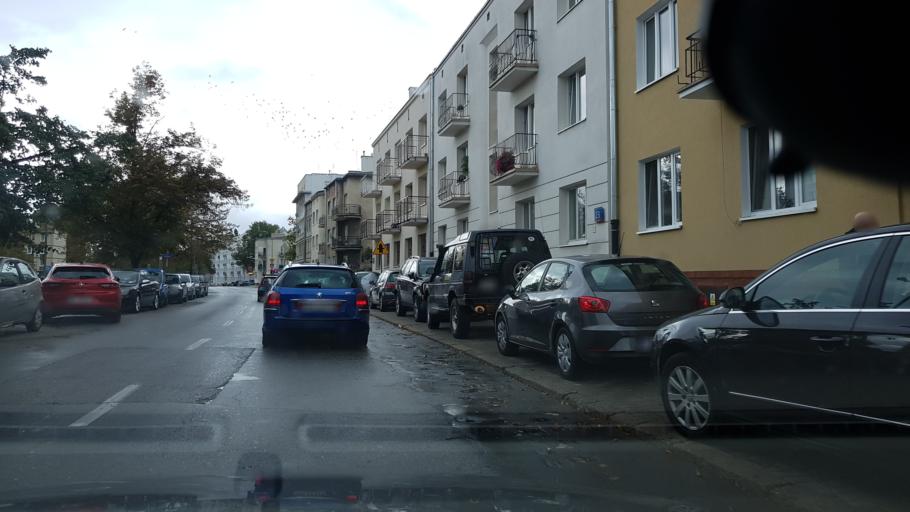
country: PL
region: Masovian Voivodeship
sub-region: Warszawa
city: Bielany
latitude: 52.2801
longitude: 20.9570
